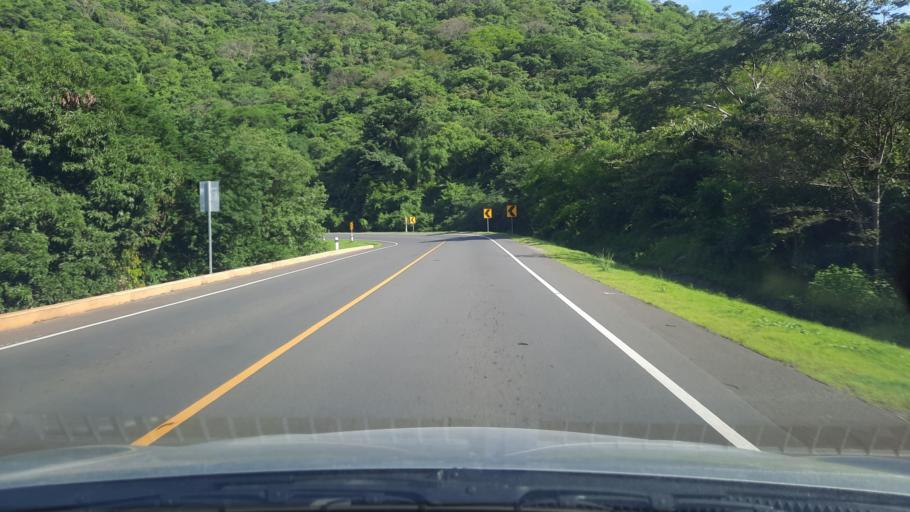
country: NI
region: Leon
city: Telica
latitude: 12.6914
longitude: -86.8569
